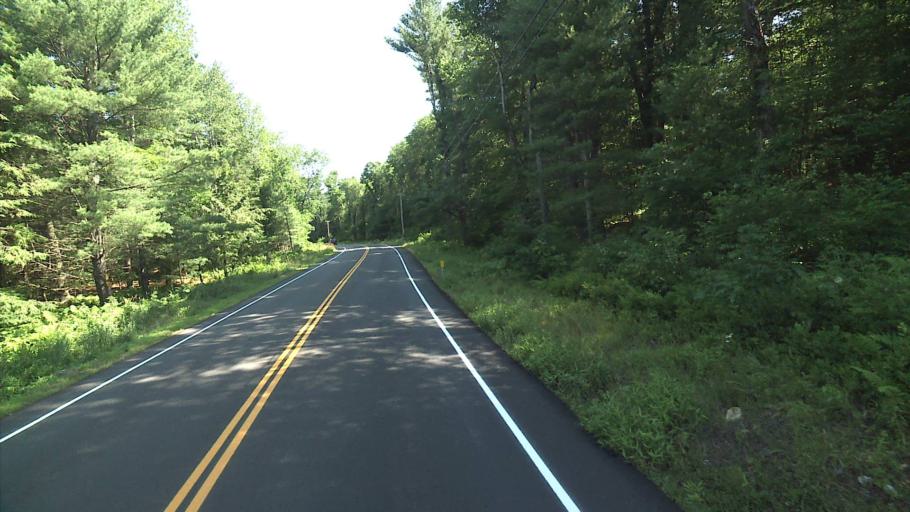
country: US
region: Connecticut
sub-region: Litchfield County
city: Terryville
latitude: 41.7238
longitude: -73.0139
